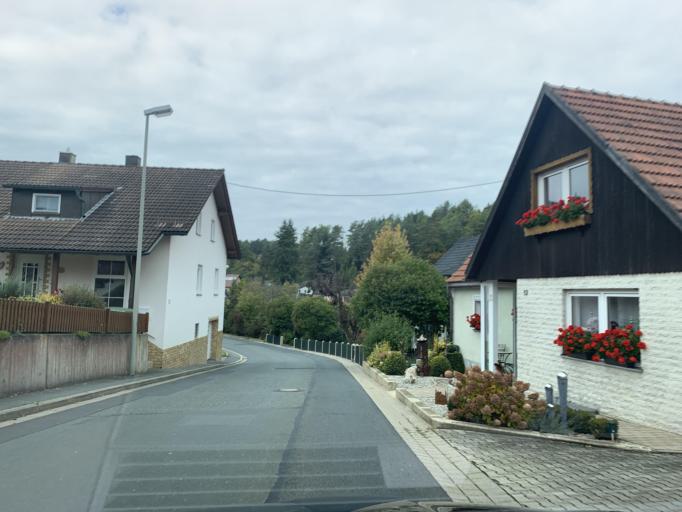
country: DE
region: Bavaria
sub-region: Upper Franconia
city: Pottenstein
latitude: 49.7372
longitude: 11.4172
